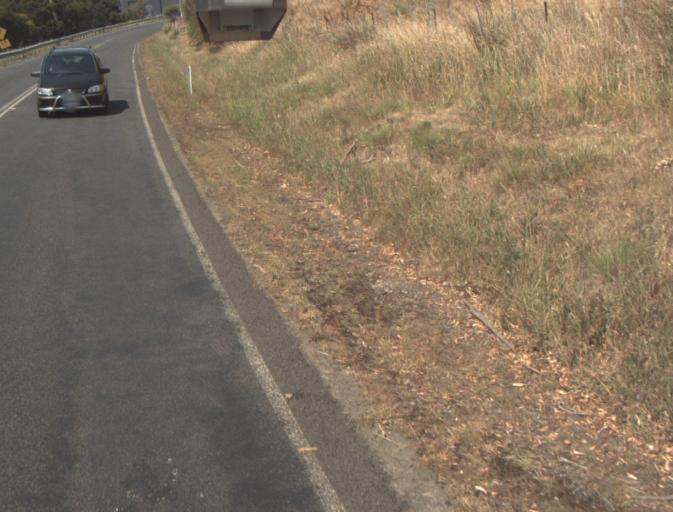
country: AU
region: Tasmania
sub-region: Launceston
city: Summerhill
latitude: -41.4954
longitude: 147.1718
